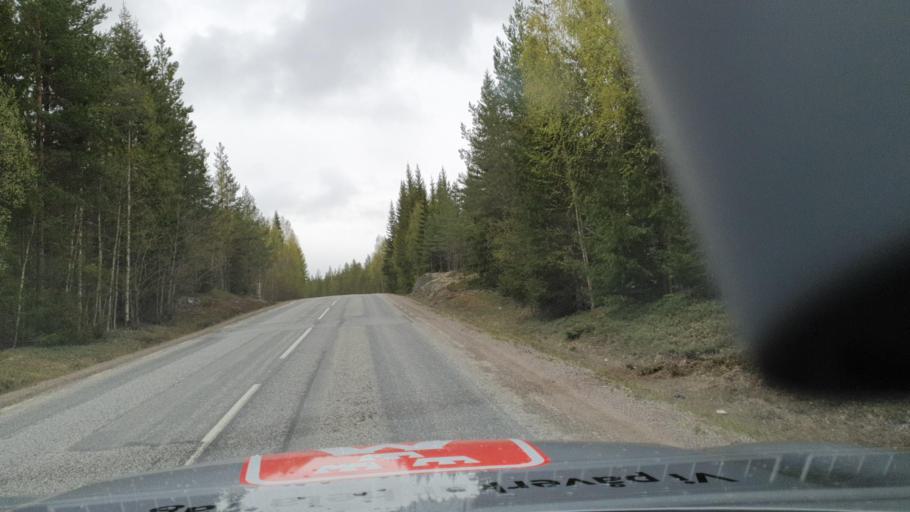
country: SE
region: Vaesterbotten
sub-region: Asele Kommun
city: Asele
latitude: 63.6709
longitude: 17.2560
